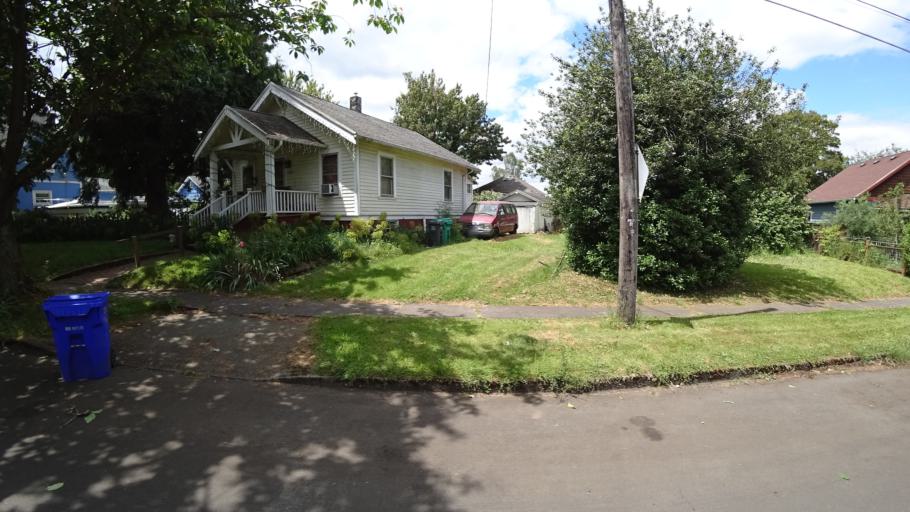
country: US
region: Oregon
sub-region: Multnomah County
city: Portland
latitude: 45.5851
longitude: -122.7204
